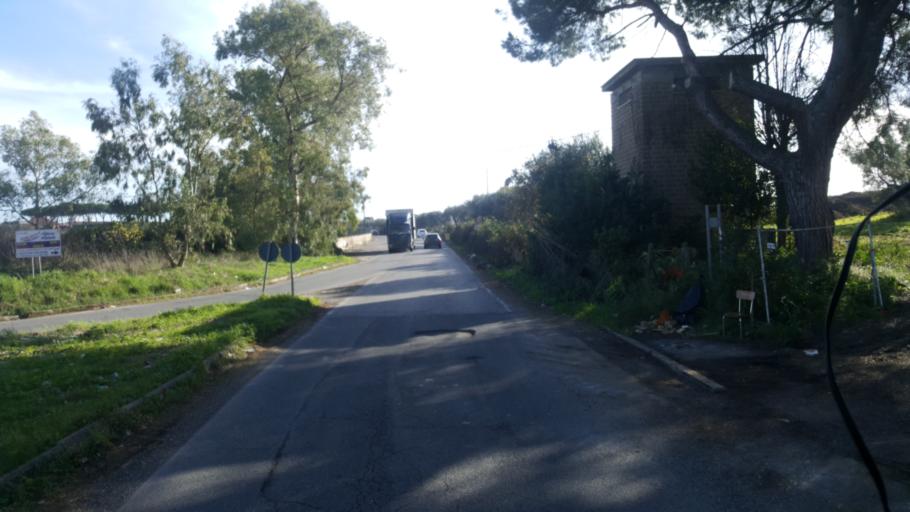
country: IT
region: Latium
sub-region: Citta metropolitana di Roma Capitale
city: Mantiglia di Ardea
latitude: 41.6917
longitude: 12.5960
